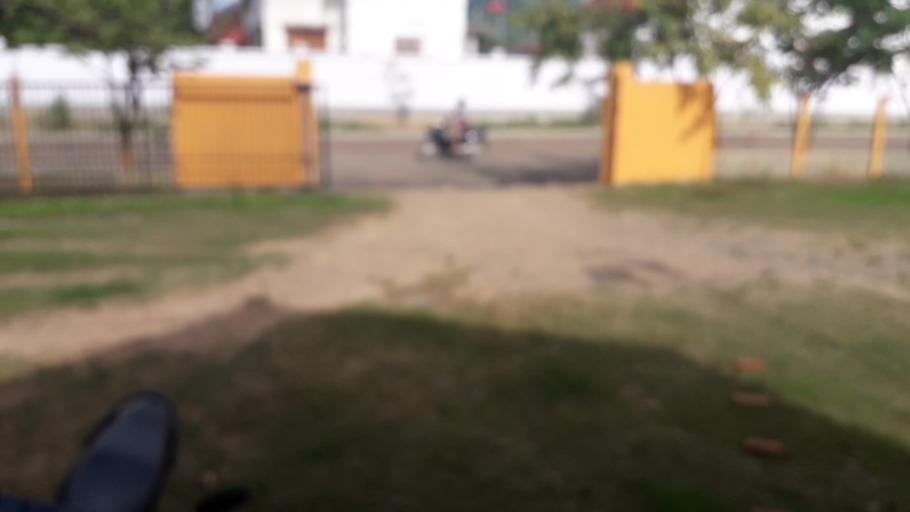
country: LA
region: Loungnamtha
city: Muang Nale
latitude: 20.1482
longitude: 101.4661
